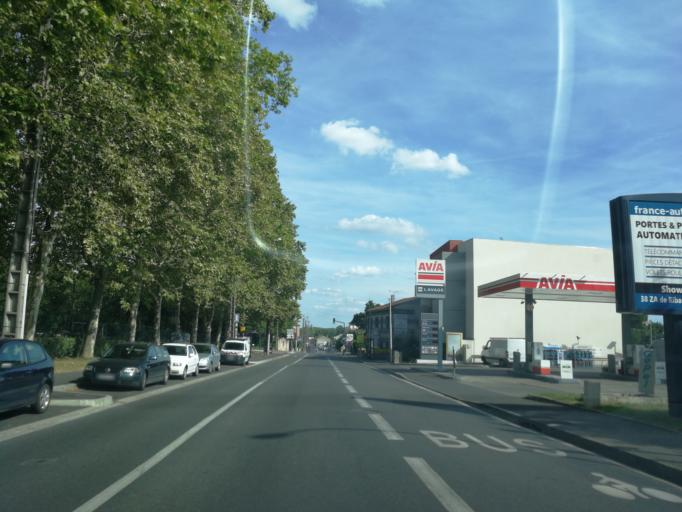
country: FR
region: Midi-Pyrenees
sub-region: Departement de la Haute-Garonne
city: Ramonville-Saint-Agne
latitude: 43.5761
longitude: 1.4879
